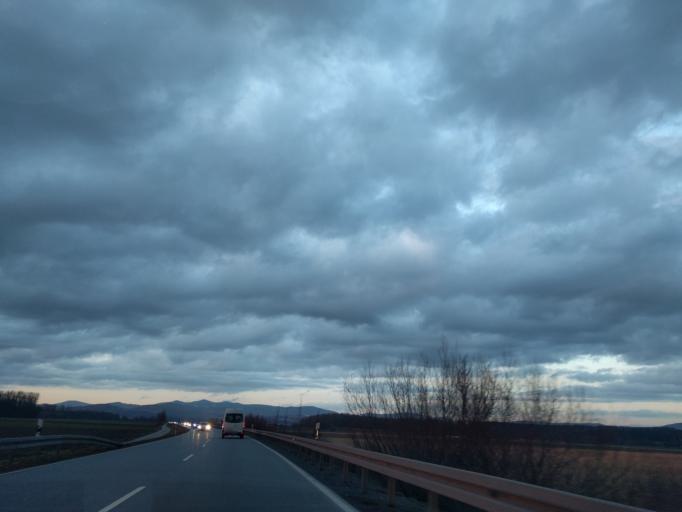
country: DE
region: Bavaria
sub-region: Lower Bavaria
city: Winzer
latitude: 48.7324
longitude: 13.0623
